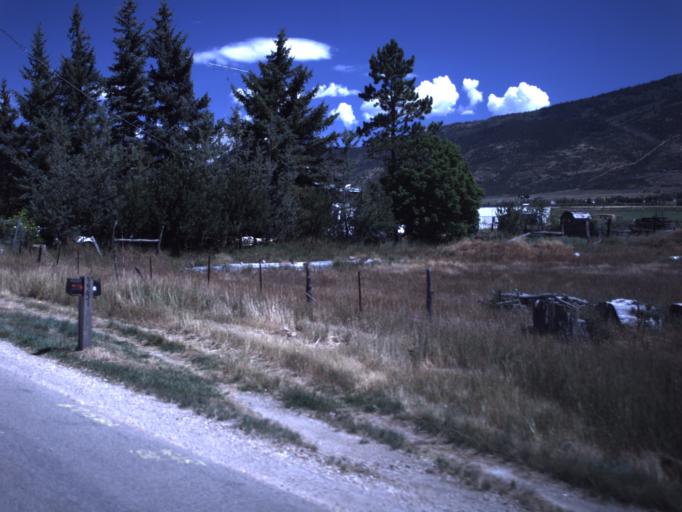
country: US
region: Utah
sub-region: Summit County
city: Kamas
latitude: 40.6769
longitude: -111.2809
